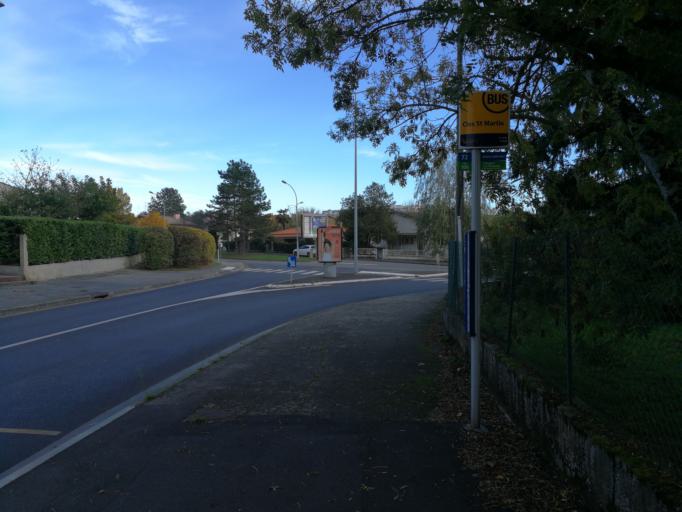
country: FR
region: Midi-Pyrenees
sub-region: Departement de la Haute-Garonne
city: Balma
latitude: 43.5972
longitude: 1.5030
